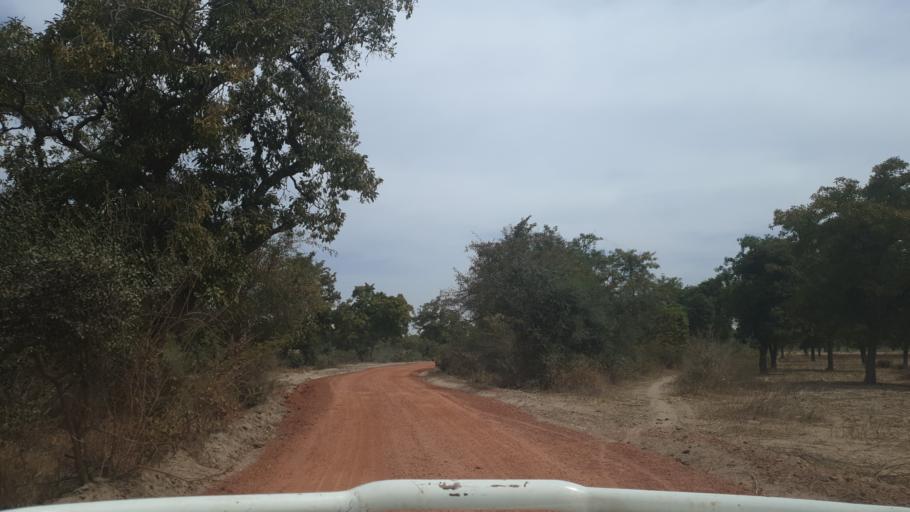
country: ML
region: Sikasso
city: Yorosso
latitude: 12.2347
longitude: -4.7457
